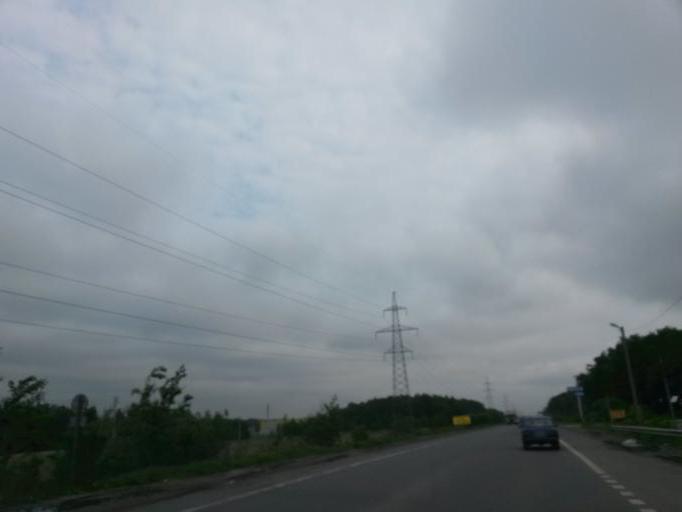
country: RU
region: Moskovskaya
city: Shcherbinka
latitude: 55.4945
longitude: 37.5819
